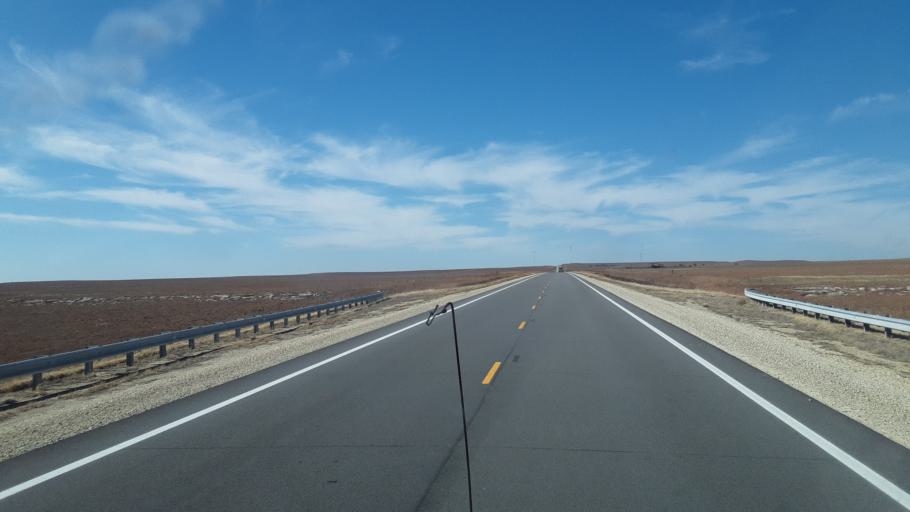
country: US
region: Kansas
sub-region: Chase County
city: Cottonwood Falls
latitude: 38.3626
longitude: -96.6957
